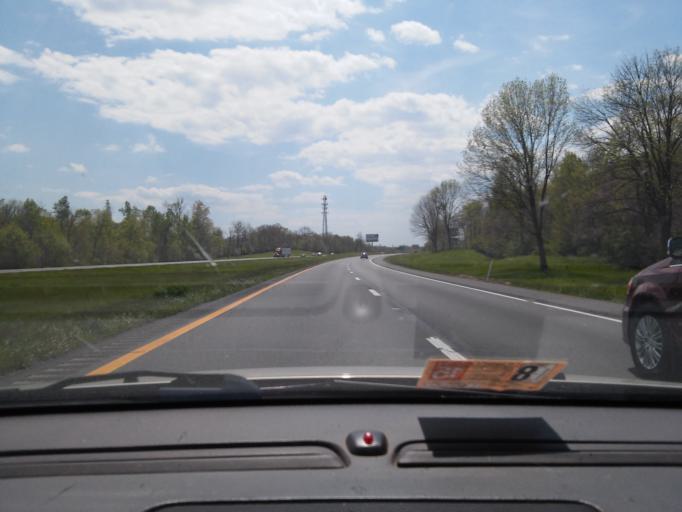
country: US
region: West Virginia
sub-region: Berkeley County
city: Inwood
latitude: 39.3825
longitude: -78.0306
